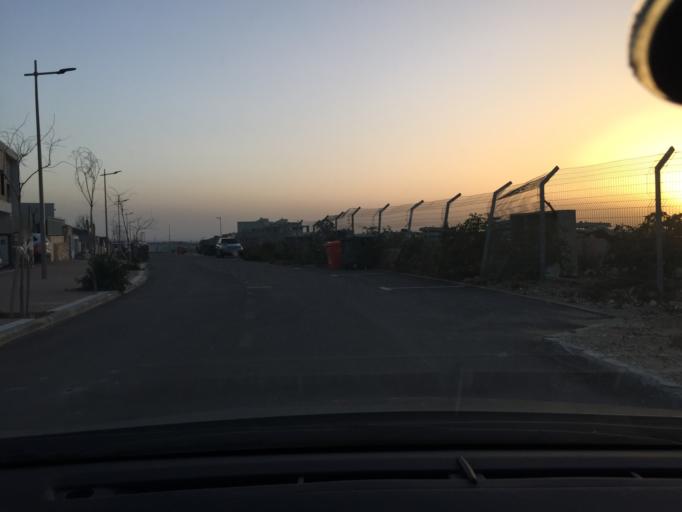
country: PS
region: West Bank
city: Rafat
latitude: 32.0686
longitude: 35.0472
